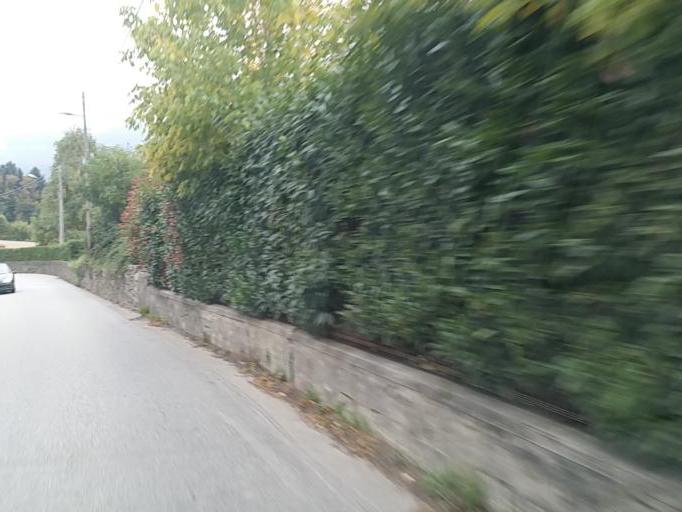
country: IT
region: Piedmont
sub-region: Provincia di Novara
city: Orta San Giulio
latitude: 45.7971
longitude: 8.4210
